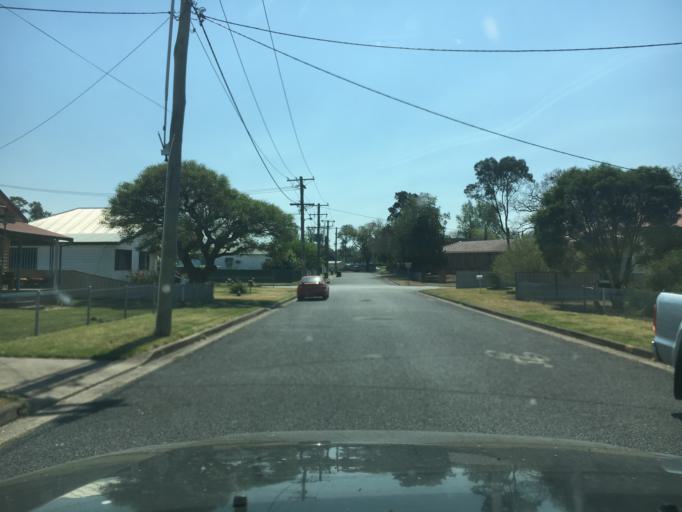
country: AU
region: New South Wales
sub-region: Singleton
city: Singleton
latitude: -32.5606
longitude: 151.1769
